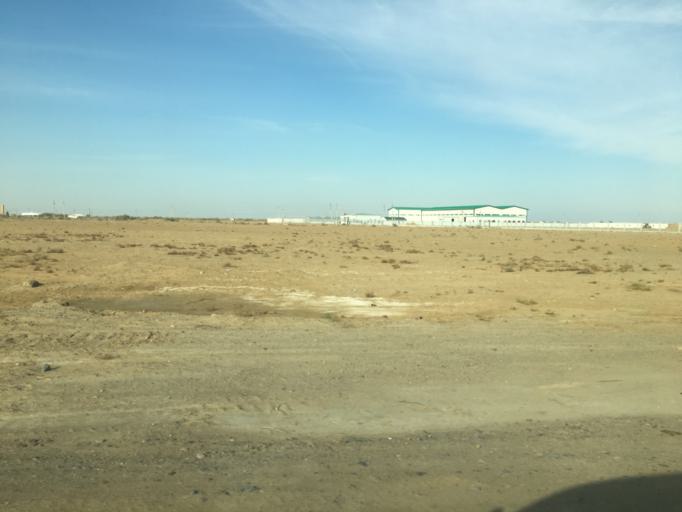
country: TM
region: Mary
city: Mary
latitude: 37.6022
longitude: 61.6106
